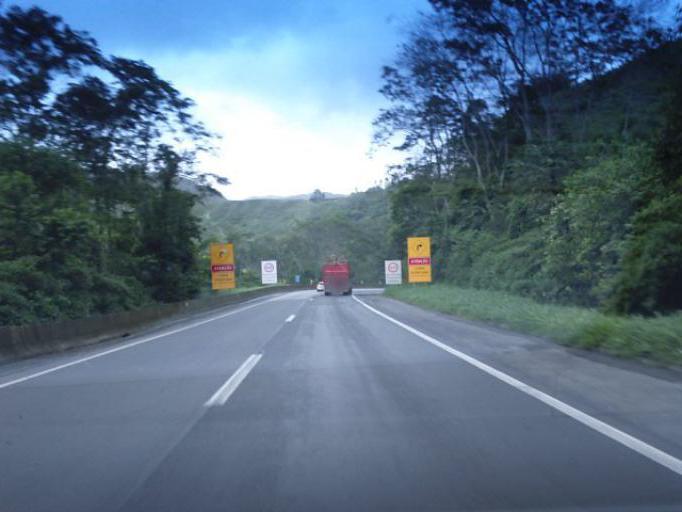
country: BR
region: Sao Paulo
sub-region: Cajati
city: Cajati
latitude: -24.8489
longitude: -48.2121
